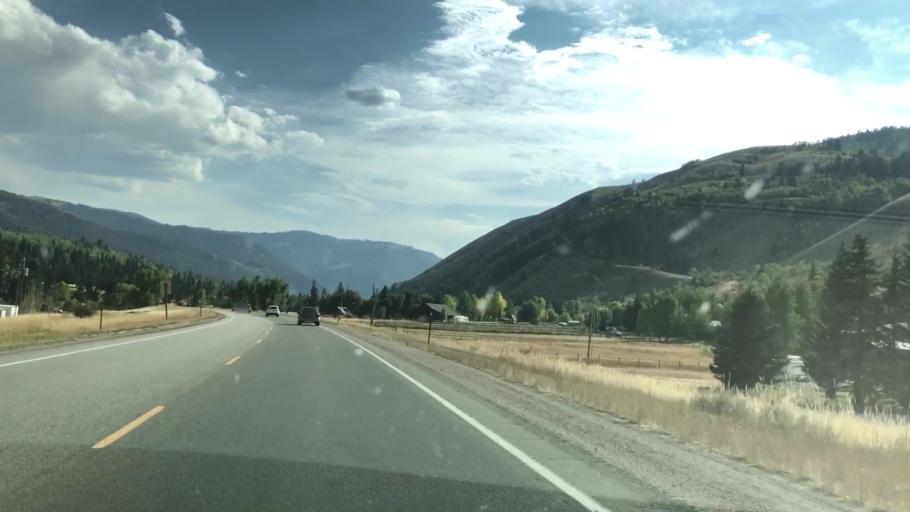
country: US
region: Wyoming
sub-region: Teton County
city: Hoback
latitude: 43.3479
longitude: -110.7216
